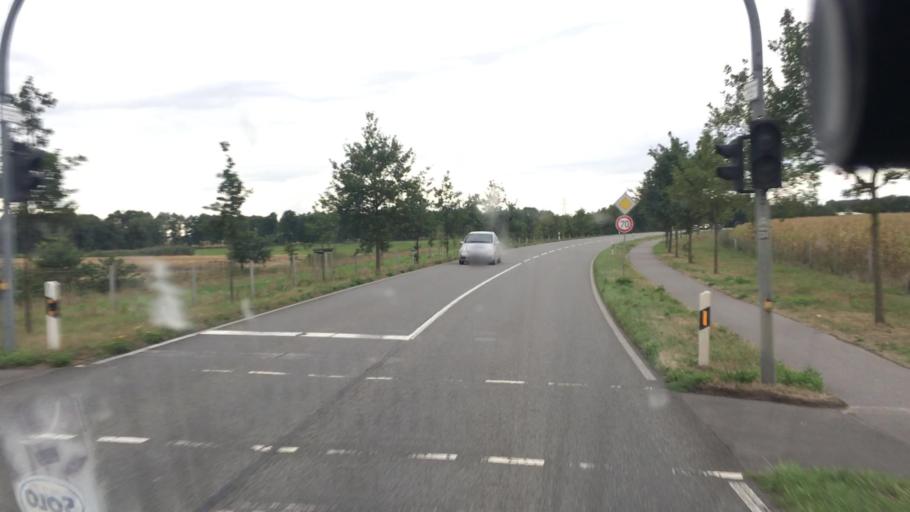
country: DE
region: Lower Saxony
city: Lohne
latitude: 52.6510
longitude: 8.2032
